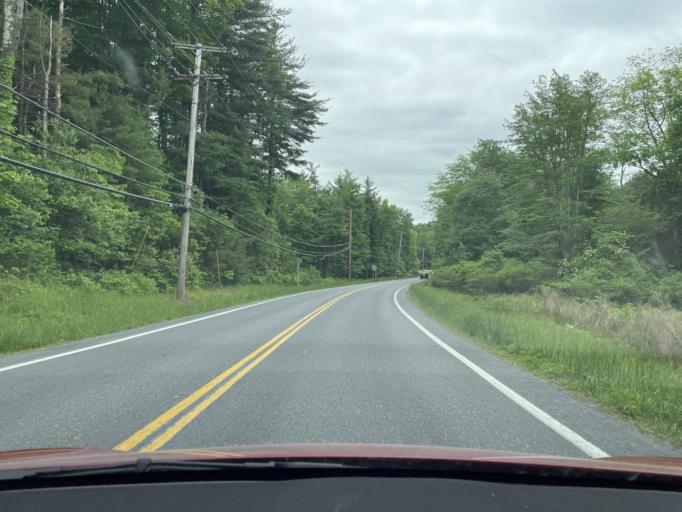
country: US
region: New York
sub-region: Ulster County
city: West Hurley
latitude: 42.0207
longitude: -74.1054
